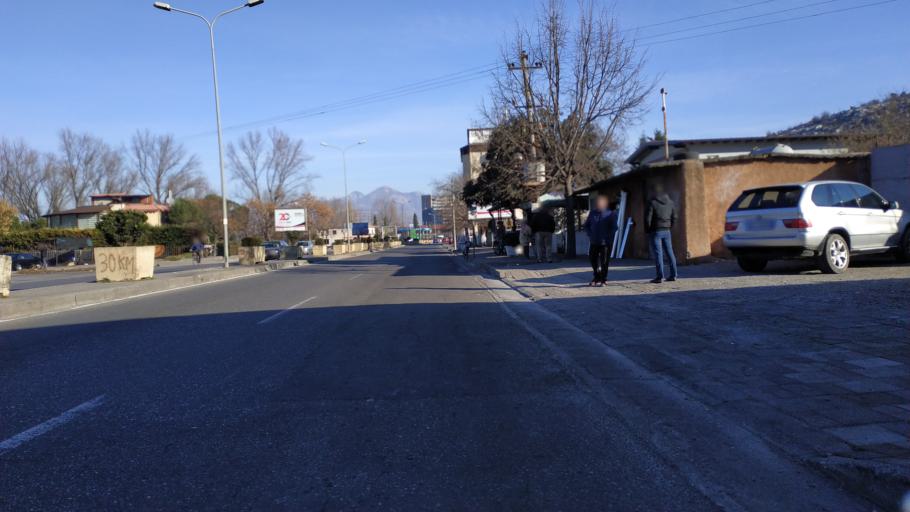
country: AL
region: Shkoder
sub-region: Rrethi i Shkodres
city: Shkoder
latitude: 42.0498
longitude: 19.4935
